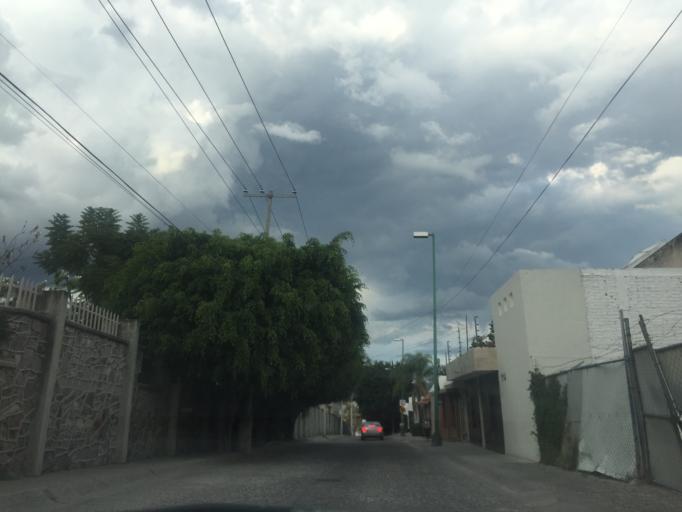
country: MX
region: Guanajuato
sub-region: Leon
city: La Ermita
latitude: 21.1510
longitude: -101.7098
